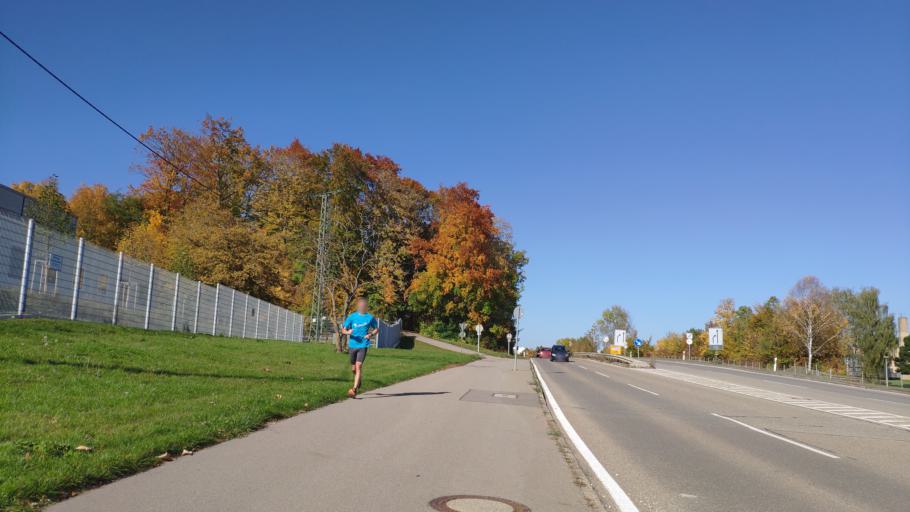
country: DE
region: Baden-Wuerttemberg
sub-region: Tuebingen Region
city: Ulm
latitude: 48.4195
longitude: 9.9832
